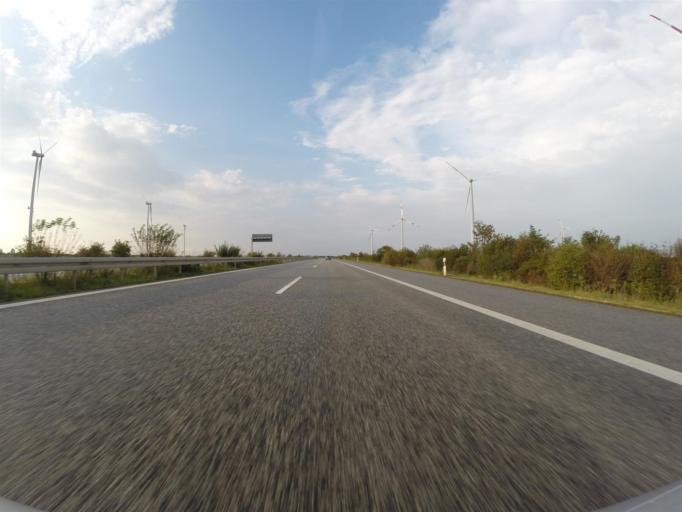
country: DE
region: Saxony-Anhalt
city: Holleben
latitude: 51.4291
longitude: 11.8646
